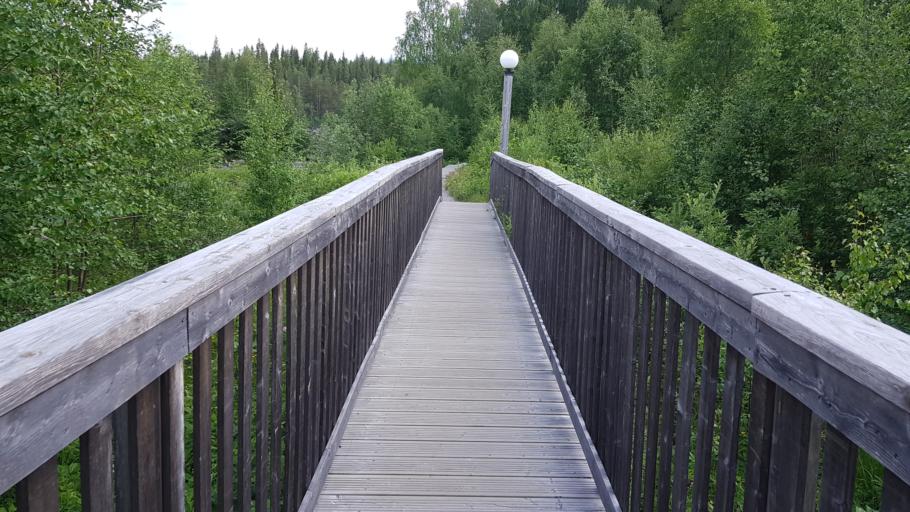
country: SE
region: Norrbotten
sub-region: Alvsbyns Kommun
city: AElvsbyn
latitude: 65.8552
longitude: 20.4155
